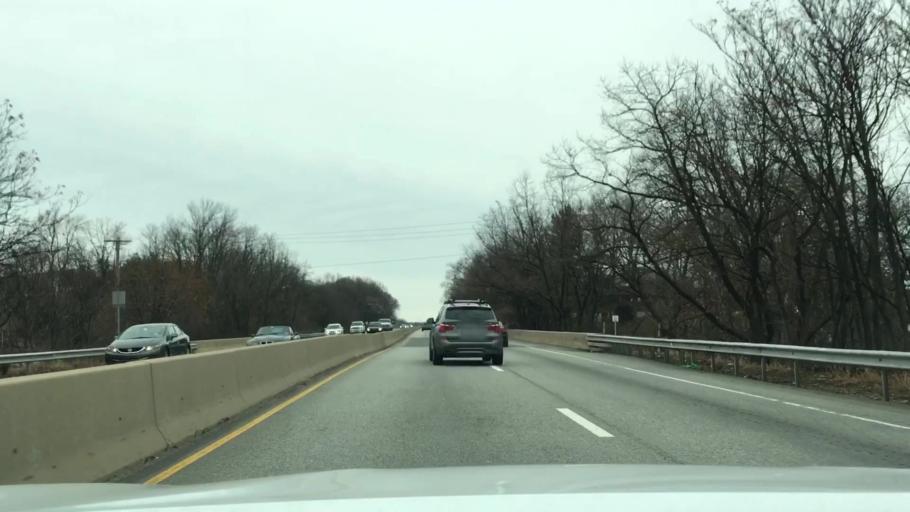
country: US
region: Pennsylvania
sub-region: Montgomery County
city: Pottstown
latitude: 40.2572
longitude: -75.6566
